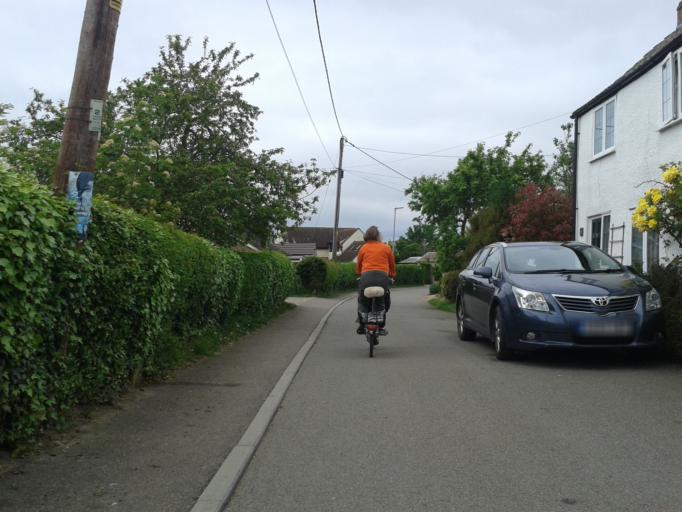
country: GB
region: England
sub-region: Cambridgeshire
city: Great Stukeley
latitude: 52.3765
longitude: -0.2678
